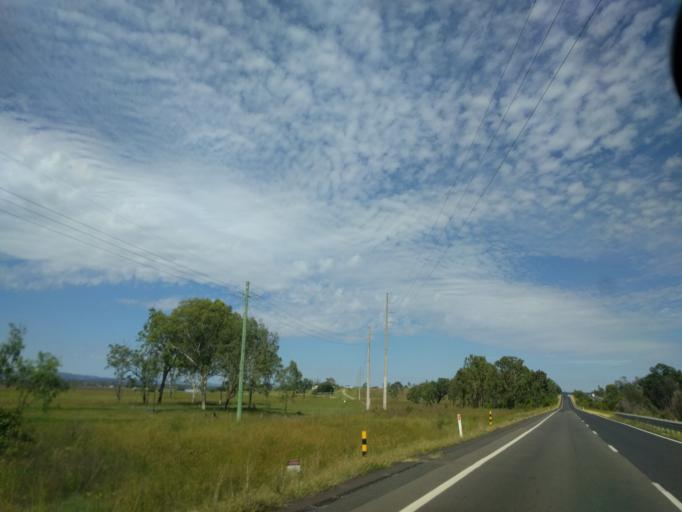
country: AU
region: Queensland
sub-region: Lockyer Valley
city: Gatton
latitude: -27.5372
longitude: 152.2716
